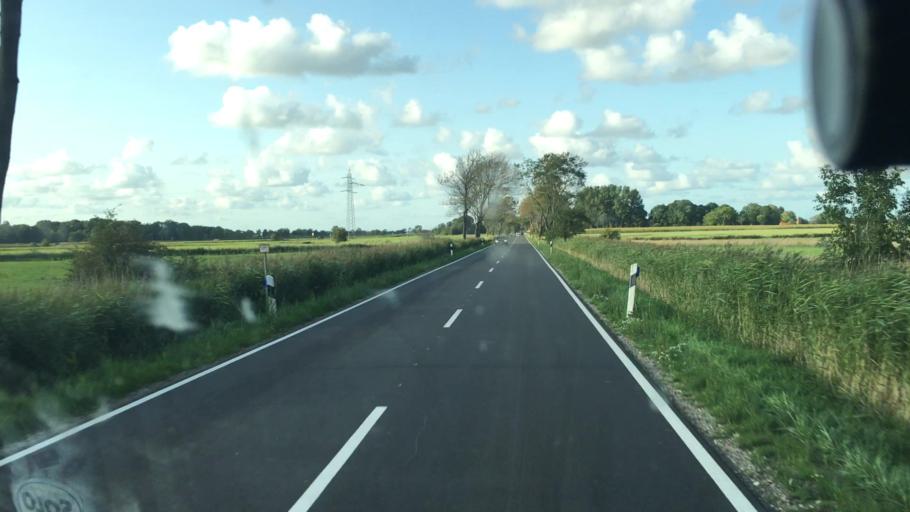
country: DE
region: Lower Saxony
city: Jever
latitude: 53.6335
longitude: 7.8614
